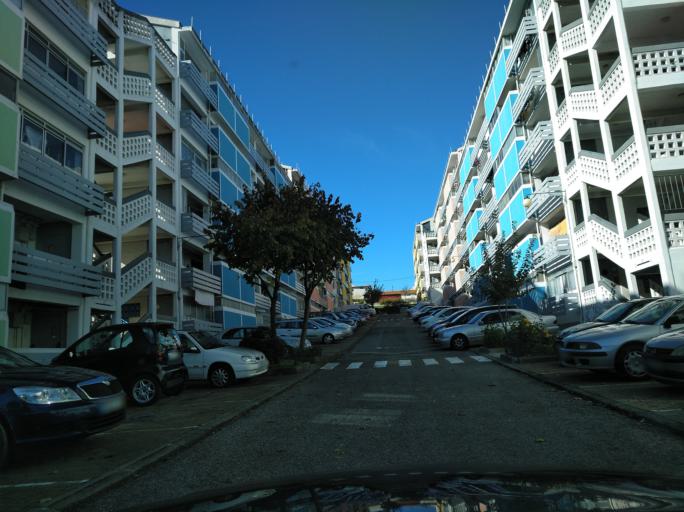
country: PT
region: Lisbon
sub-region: Loures
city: Moscavide
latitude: 38.7431
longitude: -9.1073
